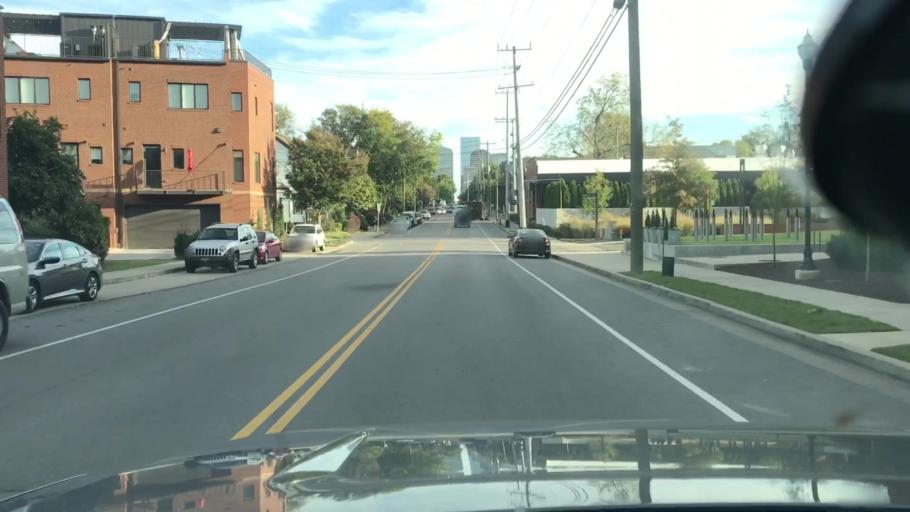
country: US
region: Tennessee
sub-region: Davidson County
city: Nashville
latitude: 36.1796
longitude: -86.7909
